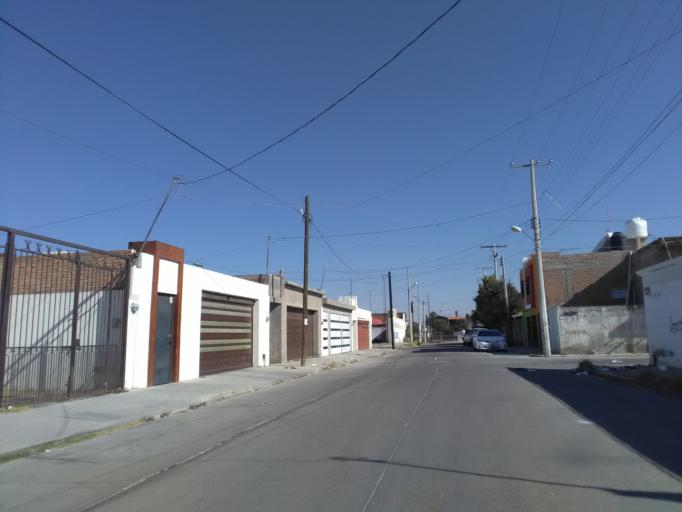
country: MX
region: Durango
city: Victoria de Durango
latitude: 24.0148
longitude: -104.6433
